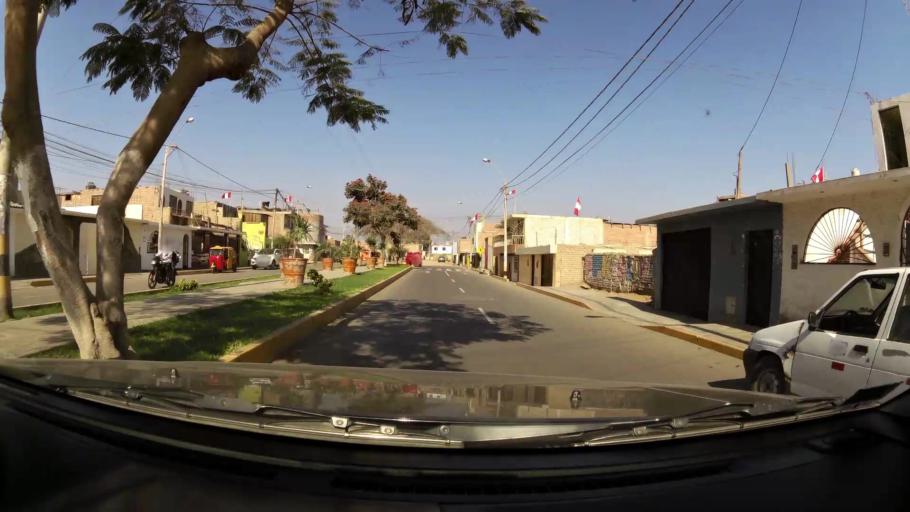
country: PE
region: Ica
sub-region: Provincia de Chincha
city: Chincha Alta
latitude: -13.4222
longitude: -76.1306
